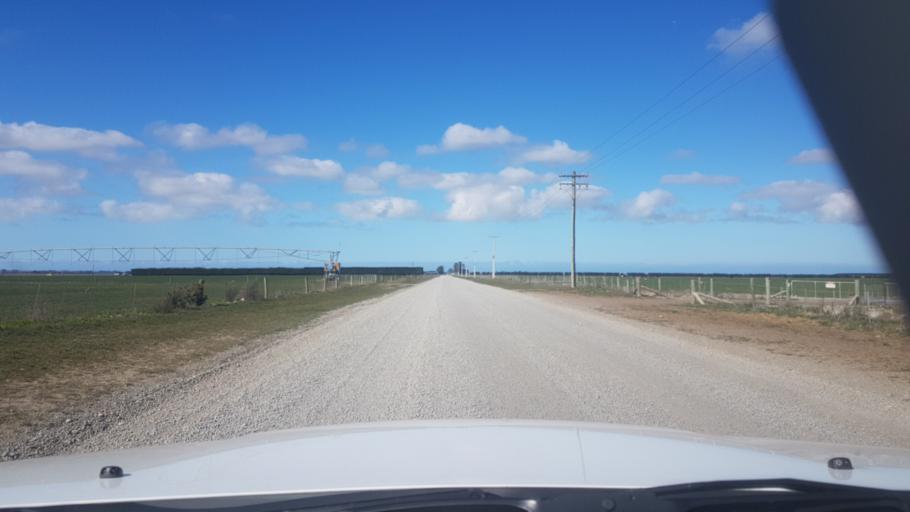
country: NZ
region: Canterbury
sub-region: Timaru District
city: Pleasant Point
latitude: -44.1222
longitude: 171.3962
